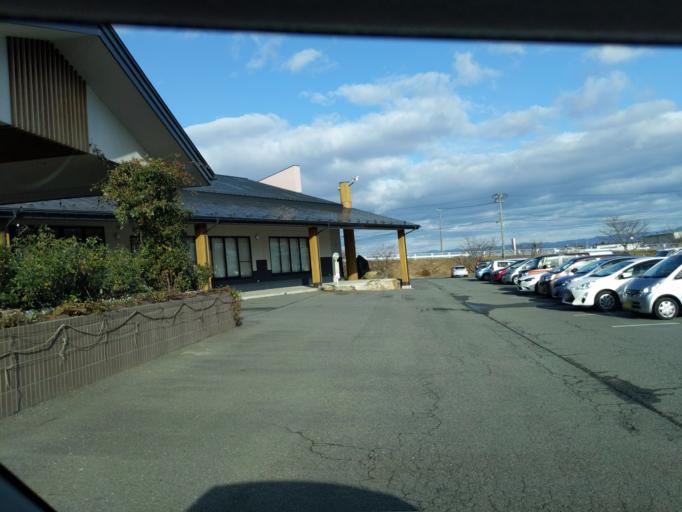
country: JP
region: Iwate
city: Mizusawa
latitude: 39.1642
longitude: 141.0906
